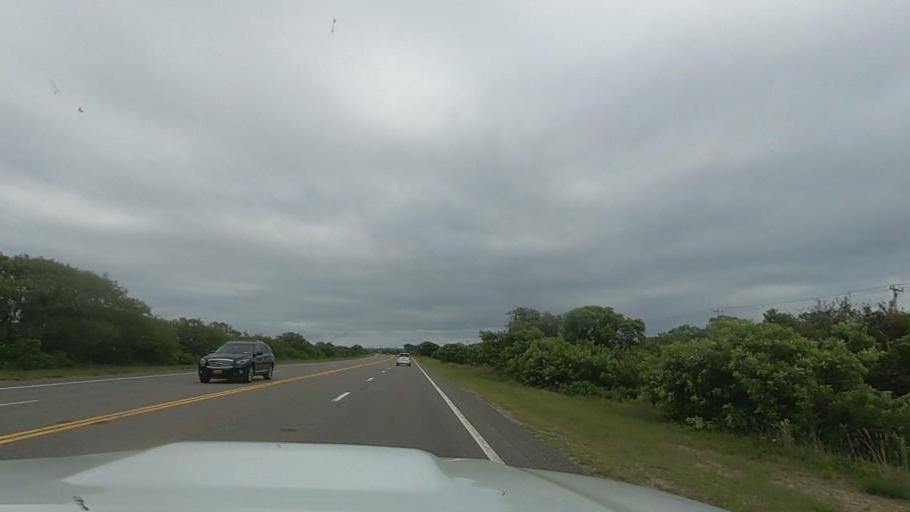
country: US
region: Massachusetts
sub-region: Barnstable County
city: Provincetown
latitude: 42.0597
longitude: -70.1391
